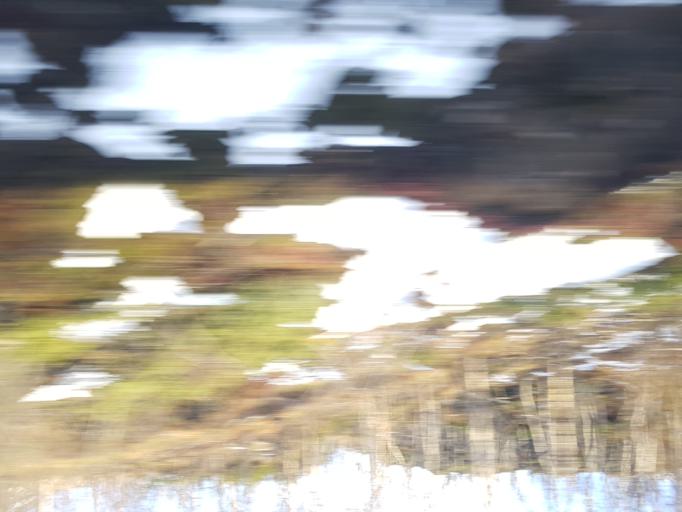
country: NO
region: Sor-Trondelag
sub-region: Oppdal
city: Oppdal
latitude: 62.3603
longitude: 9.6322
